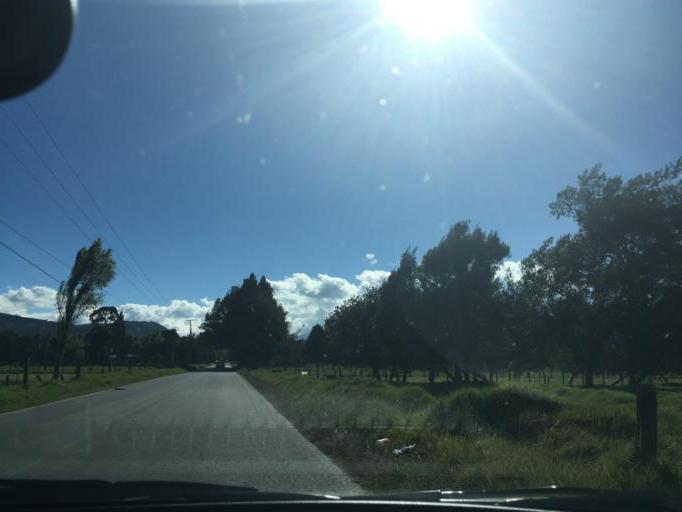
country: CO
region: Boyaca
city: Firavitoba
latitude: 5.6496
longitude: -72.9859
